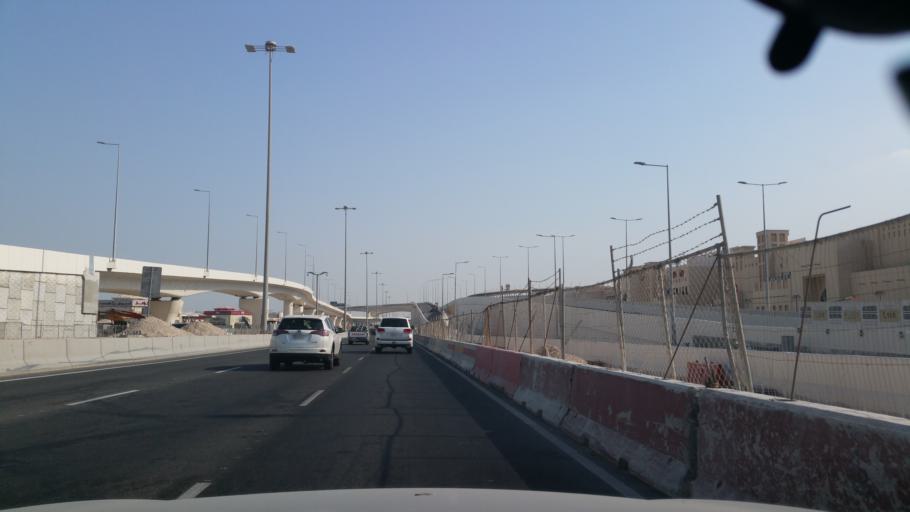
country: QA
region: Baladiyat ar Rayyan
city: Ar Rayyan
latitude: 25.3377
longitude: 51.4613
